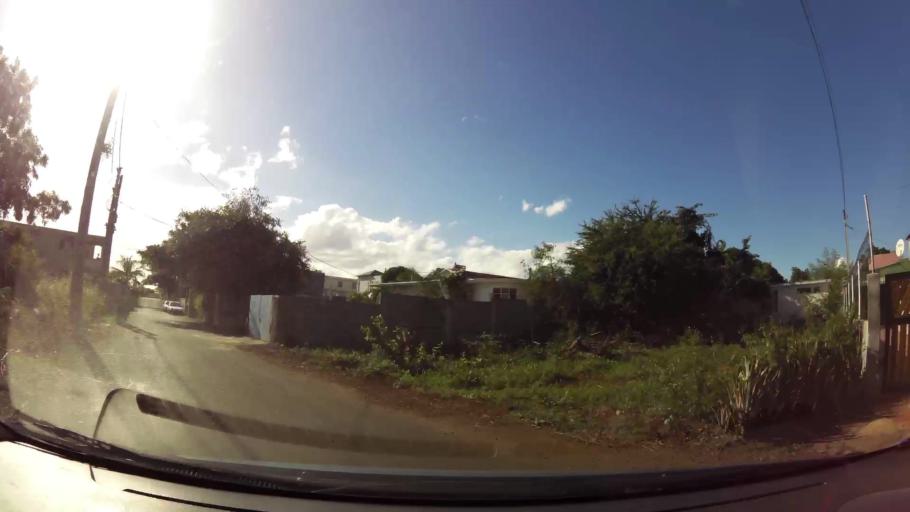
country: MU
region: Black River
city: Albion
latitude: -20.1996
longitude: 57.4124
